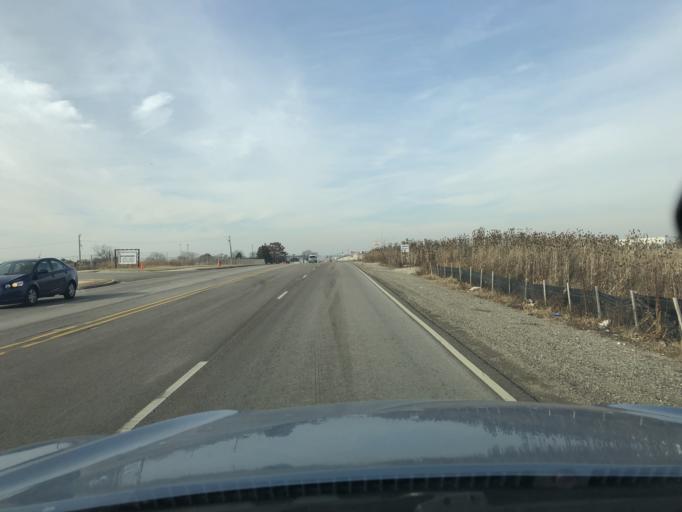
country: US
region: Illinois
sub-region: DuPage County
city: Bensenville
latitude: 41.9800
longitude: -87.9469
